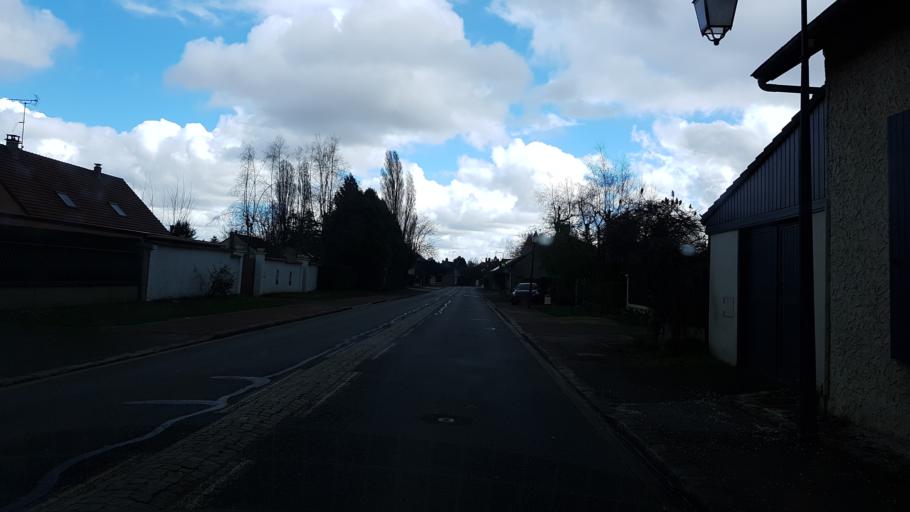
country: FR
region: Ile-de-France
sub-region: Departement des Yvelines
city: Rambouillet
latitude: 48.6162
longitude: 1.8383
